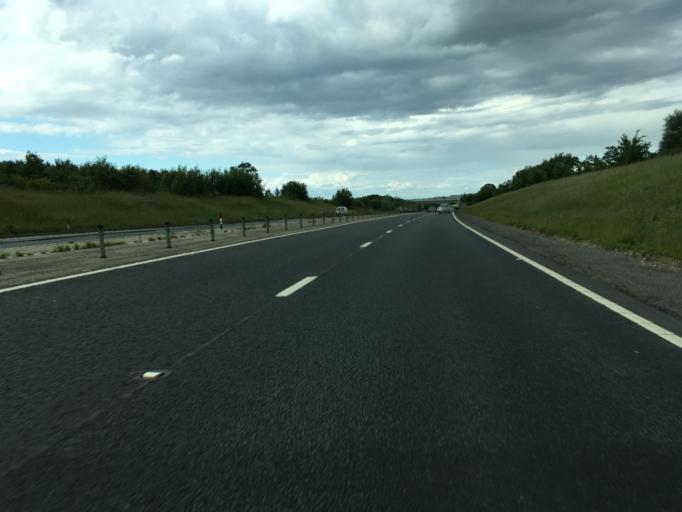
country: GB
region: England
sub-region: Central Bedfordshire
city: Leighton Buzzard
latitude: 51.9118
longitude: -0.7008
